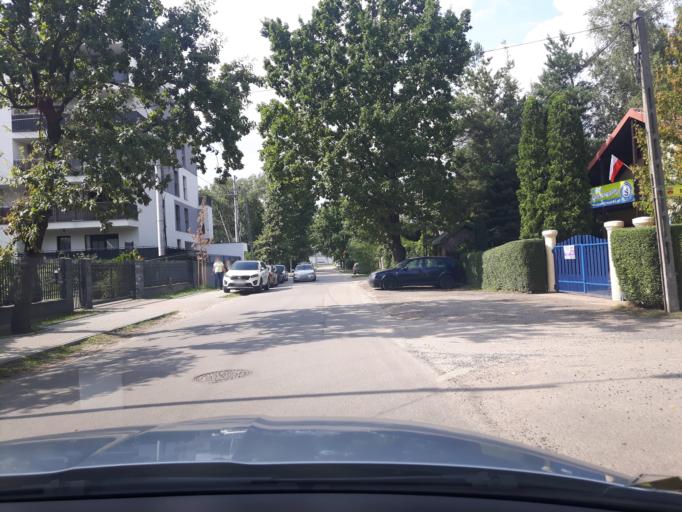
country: PL
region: Masovian Voivodeship
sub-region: Powiat wolominski
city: Marki
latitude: 52.3101
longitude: 21.0992
